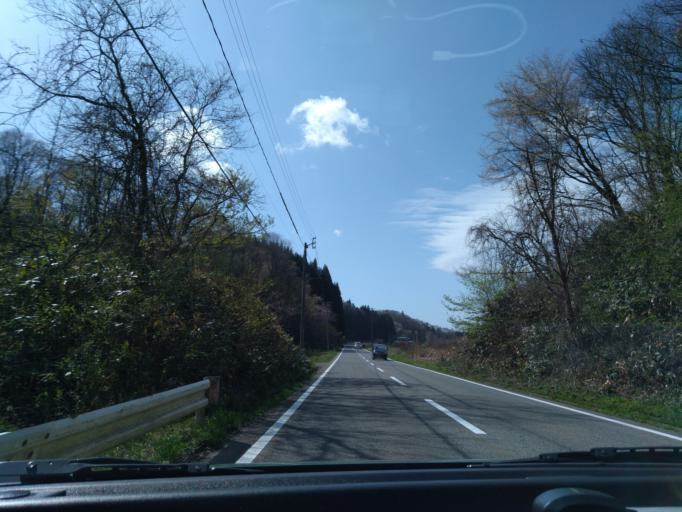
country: JP
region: Akita
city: Akita
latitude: 39.7056
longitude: 140.2114
